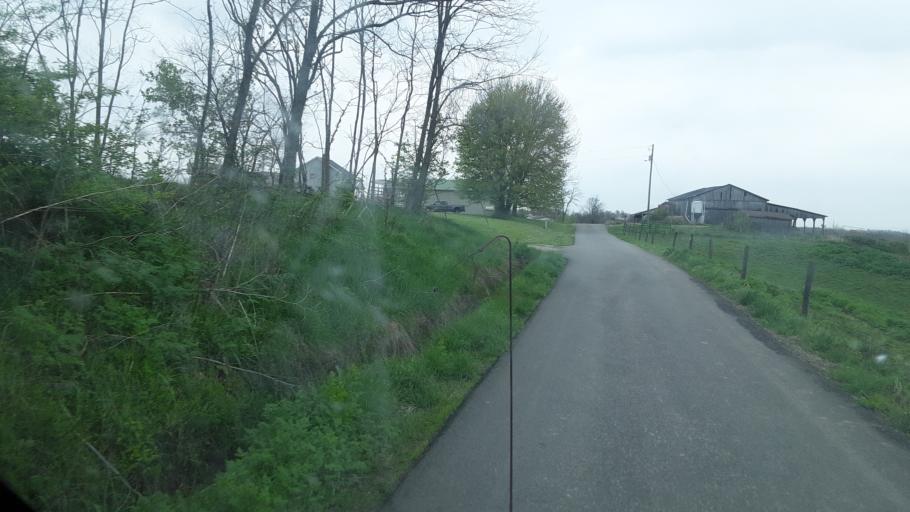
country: US
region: Kentucky
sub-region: Owen County
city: Owenton
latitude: 38.6665
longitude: -84.7820
